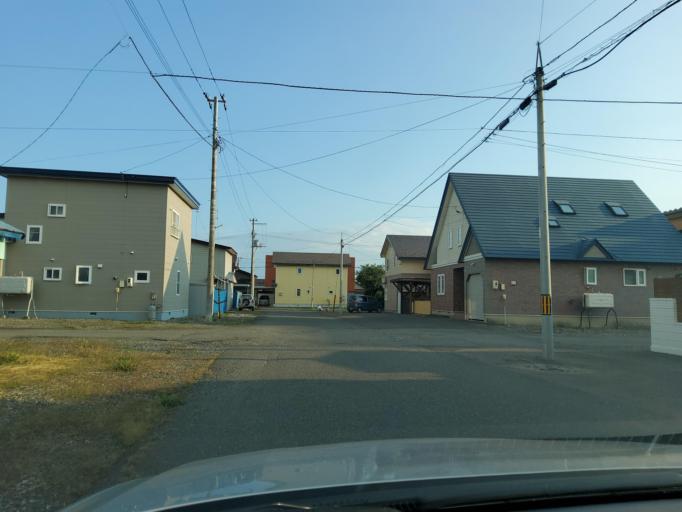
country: JP
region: Hokkaido
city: Obihiro
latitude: 42.9186
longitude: 143.1702
